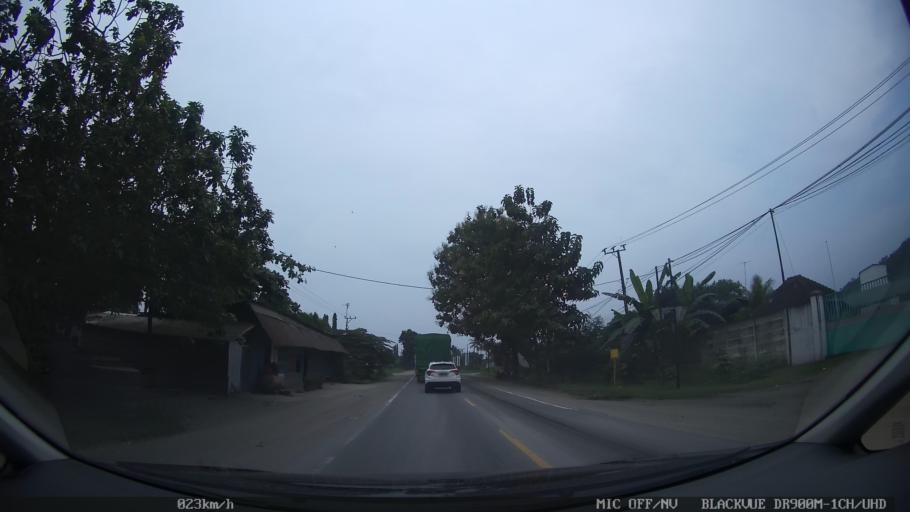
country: ID
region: Lampung
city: Panjang
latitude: -5.4325
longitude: 105.3251
